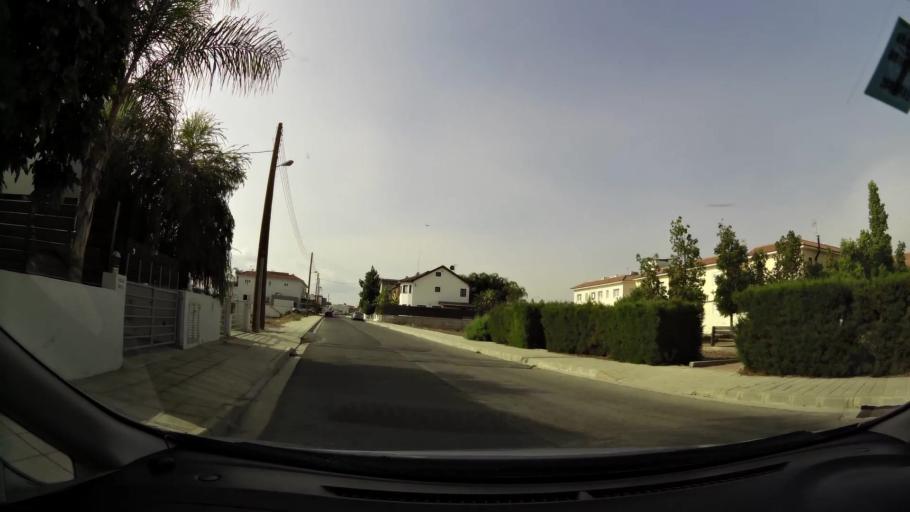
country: CY
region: Lefkosia
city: Geri
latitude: 35.0697
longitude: 33.3969
